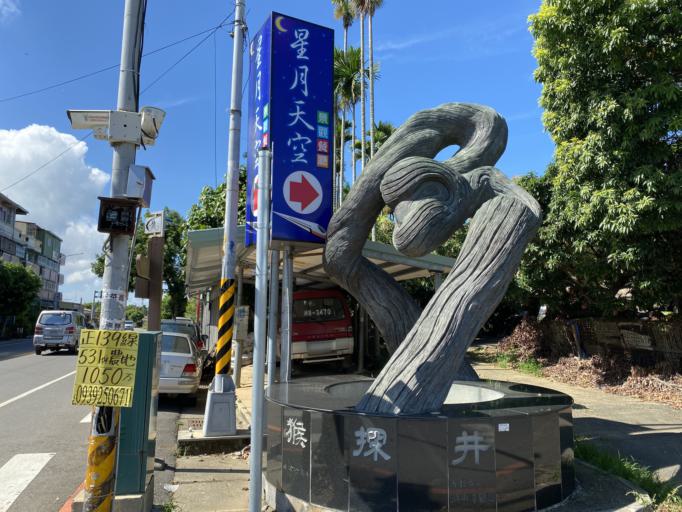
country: TW
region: Taiwan
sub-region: Nantou
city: Nantou
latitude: 23.9089
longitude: 120.6368
